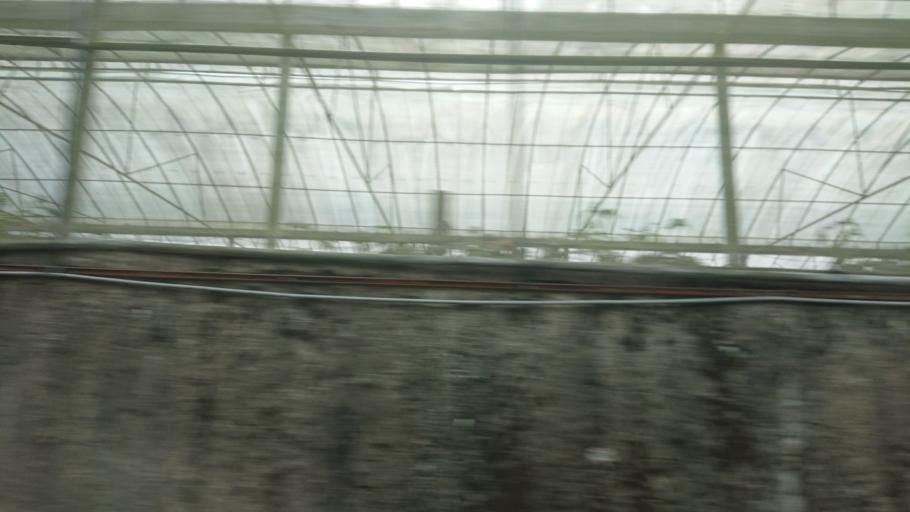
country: TW
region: Taiwan
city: Lugu
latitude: 23.5943
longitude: 120.7013
